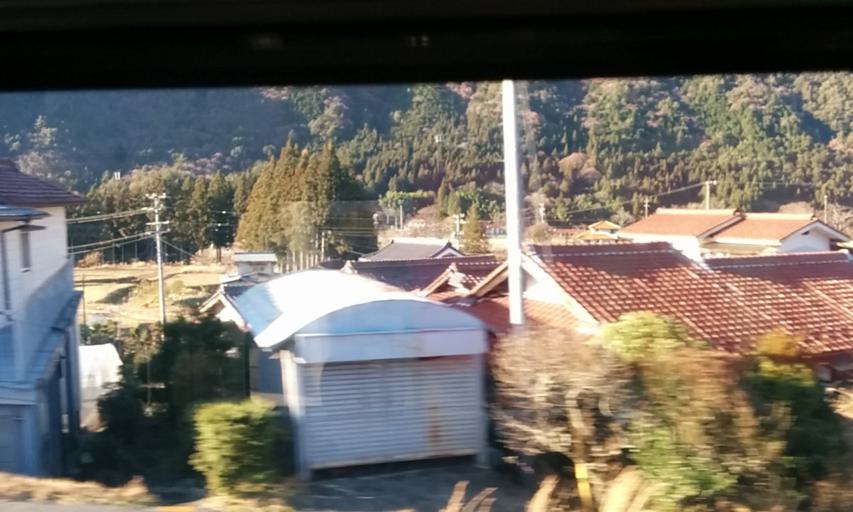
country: JP
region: Gifu
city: Nakatsugawa
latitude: 35.6706
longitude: 137.6328
